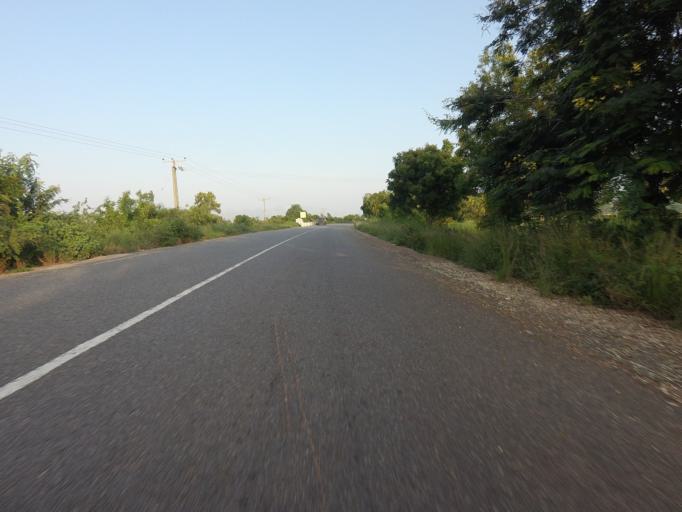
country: GH
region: Volta
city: Anloga
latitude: 5.8612
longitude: 0.7635
